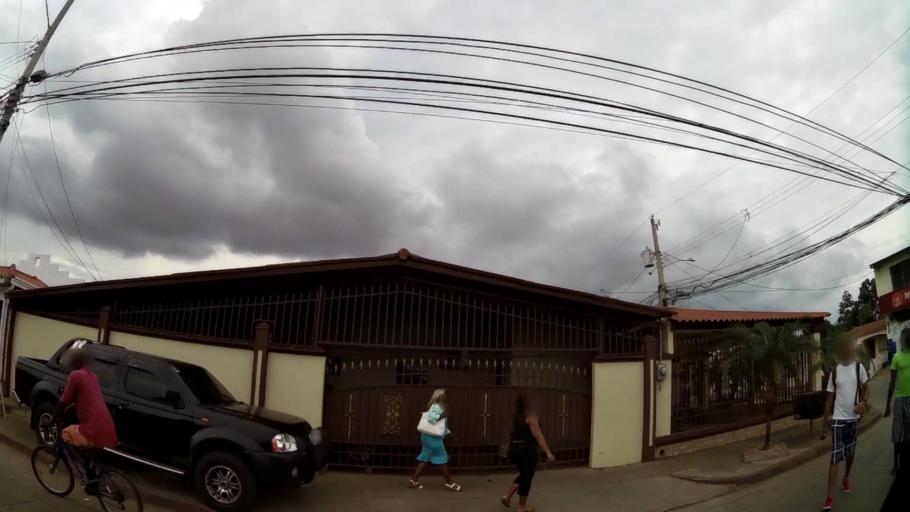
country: PA
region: Panama
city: Tocumen
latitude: 9.0419
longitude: -79.4071
